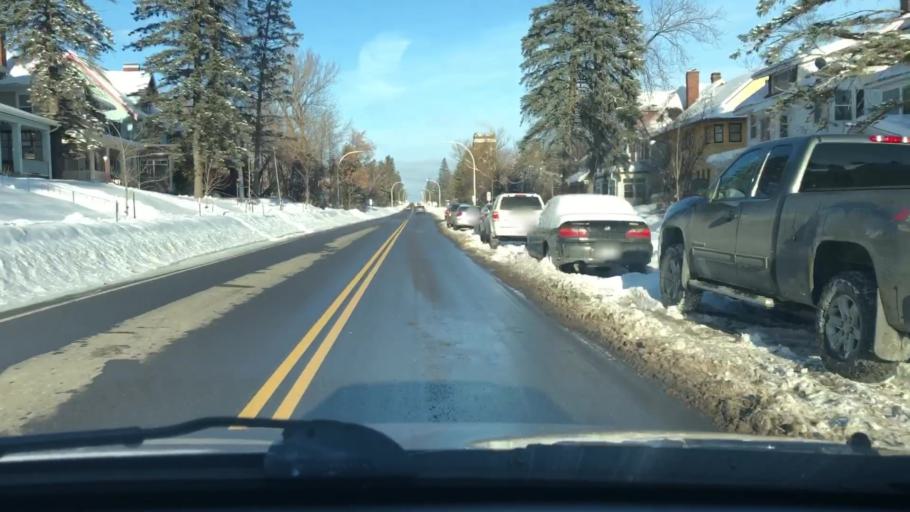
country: US
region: Minnesota
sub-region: Saint Louis County
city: Duluth
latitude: 46.8099
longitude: -92.0761
